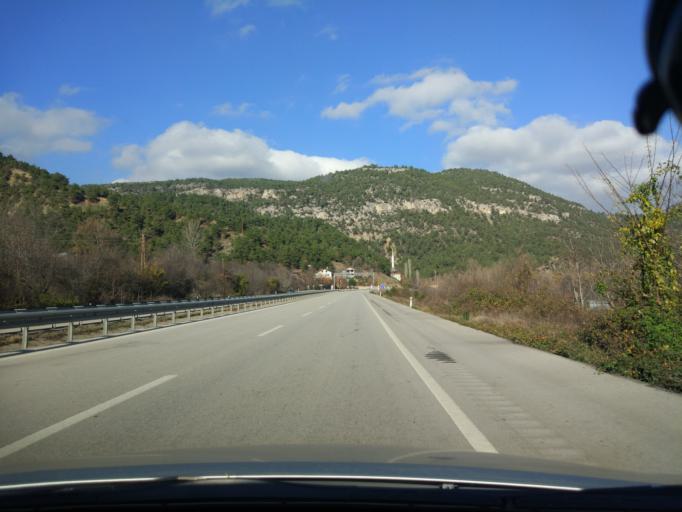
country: TR
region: Karabuk
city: Karabuk
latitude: 41.0707
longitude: 32.6563
